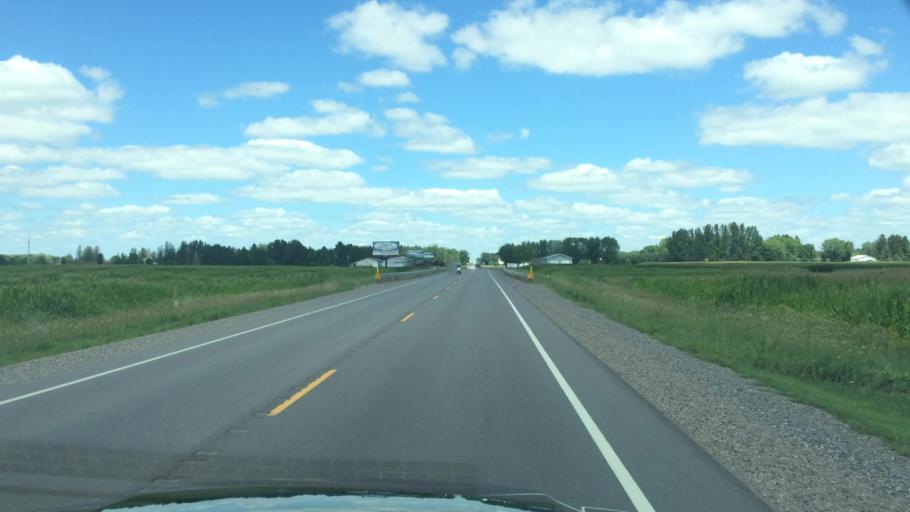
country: US
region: Wisconsin
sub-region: Clark County
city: Abbotsford
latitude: 45.0124
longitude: -90.3153
